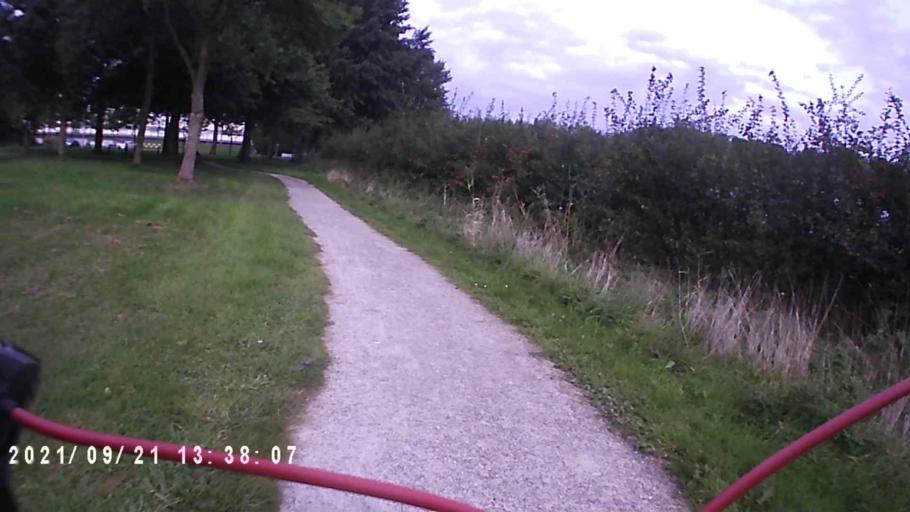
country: NL
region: Groningen
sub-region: Gemeente Groningen
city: Korrewegwijk
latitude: 53.2488
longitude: 6.5277
